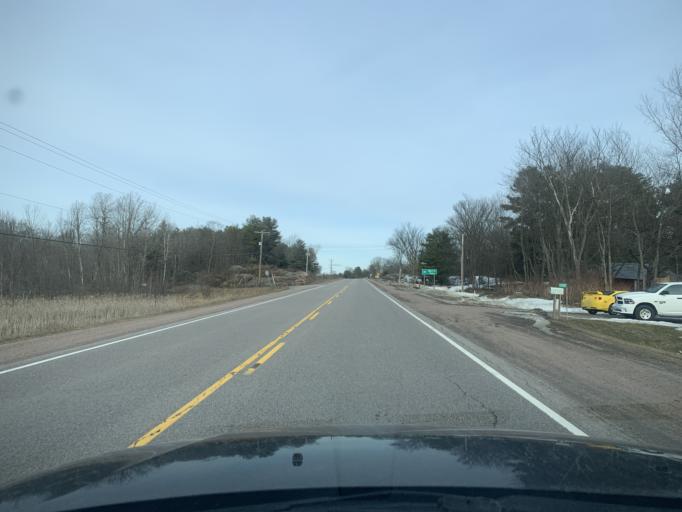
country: CA
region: Ontario
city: Greater Napanee
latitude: 44.6517
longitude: -77.1136
